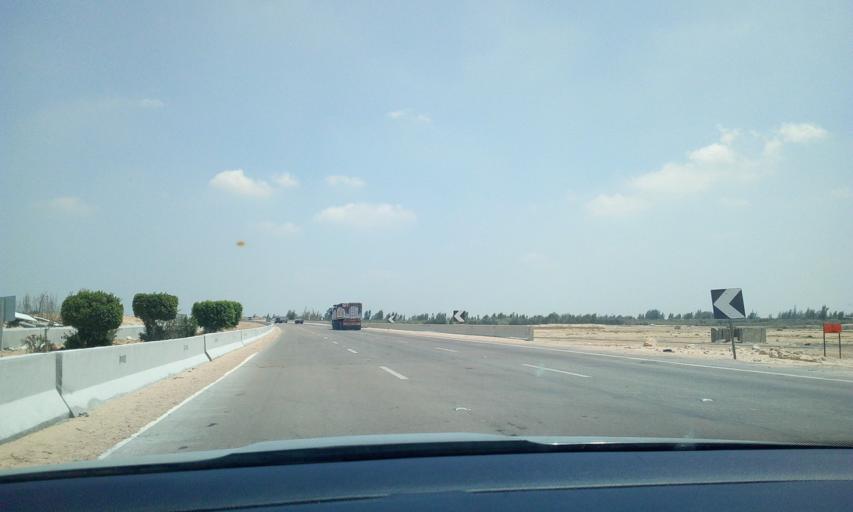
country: EG
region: Al Buhayrah
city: Beheira
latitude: 30.4865
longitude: 30.1976
